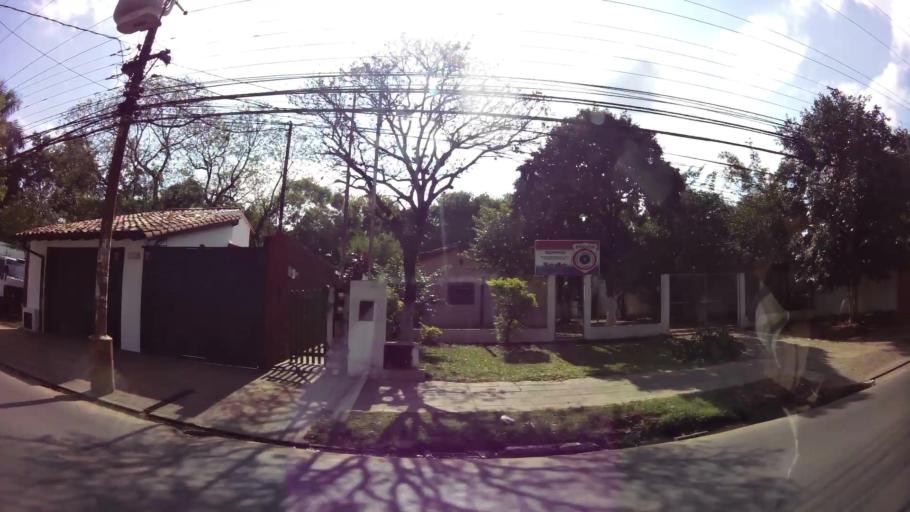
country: PY
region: Central
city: Fernando de la Mora
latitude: -25.3174
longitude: -57.5375
